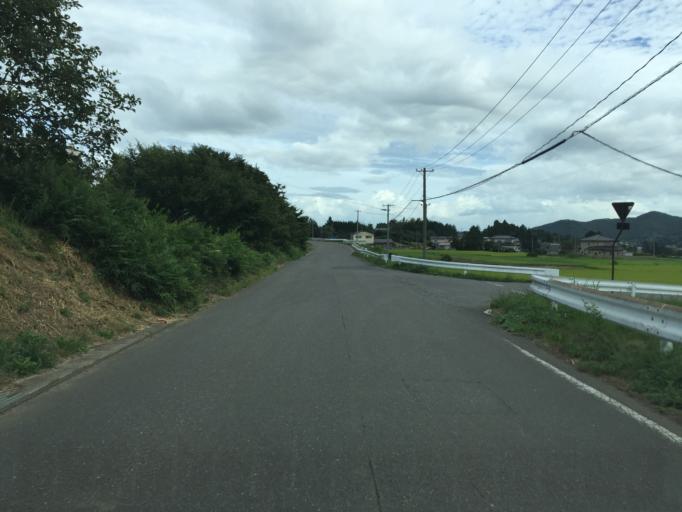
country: JP
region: Fukushima
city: Motomiya
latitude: 37.5371
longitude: 140.3604
